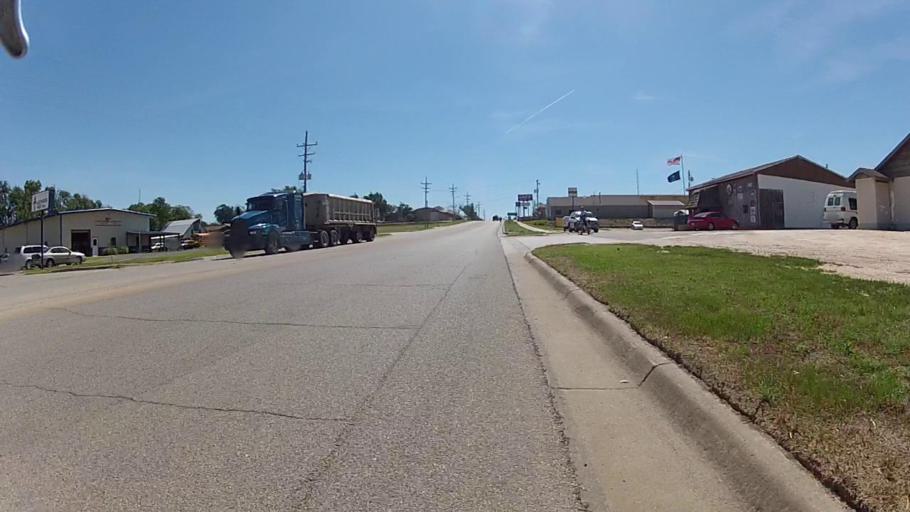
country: US
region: Kansas
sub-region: Barber County
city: Medicine Lodge
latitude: 37.2756
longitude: -98.5852
